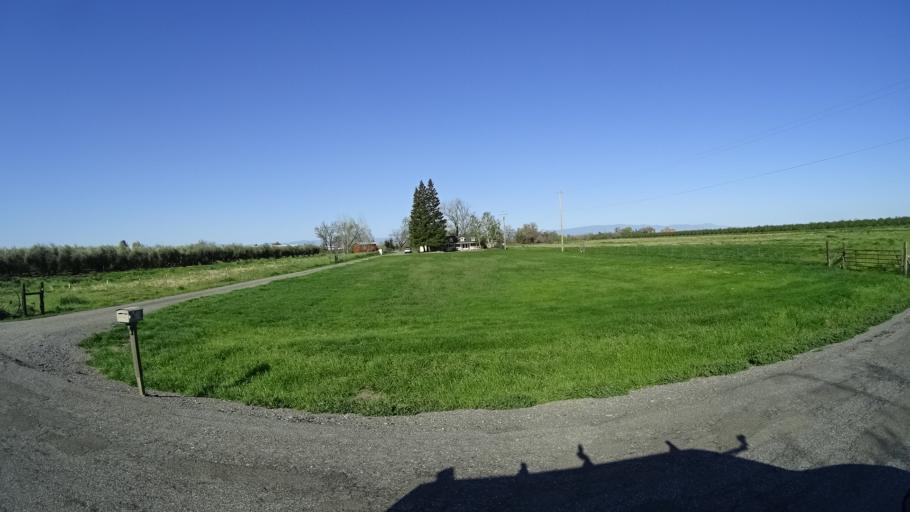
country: US
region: California
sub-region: Glenn County
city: Orland
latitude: 39.7612
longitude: -122.1322
